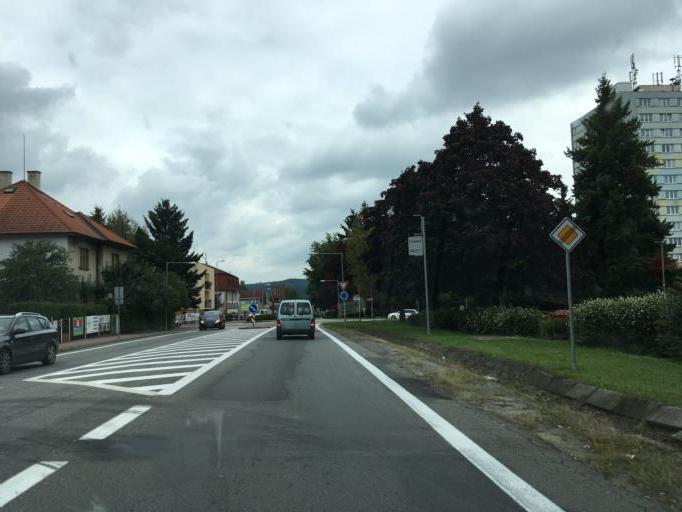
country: CZ
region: Vysocina
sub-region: Okres Pelhrimov
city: Pelhrimov
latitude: 49.4366
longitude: 15.2157
